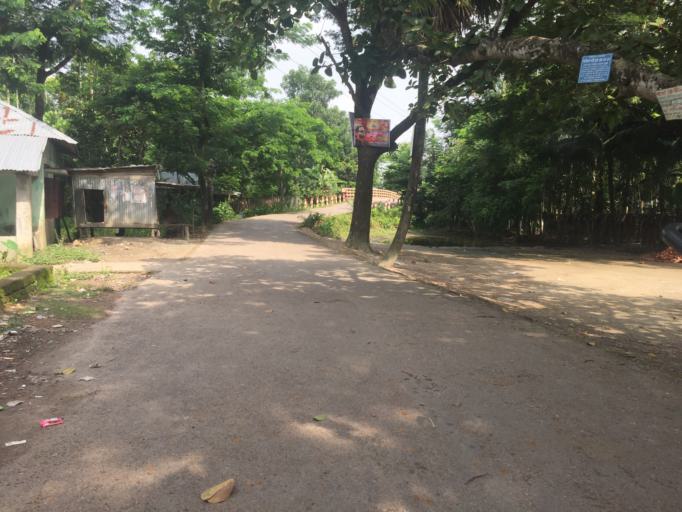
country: BD
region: Barisal
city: Mathba
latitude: 22.2612
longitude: 89.9117
